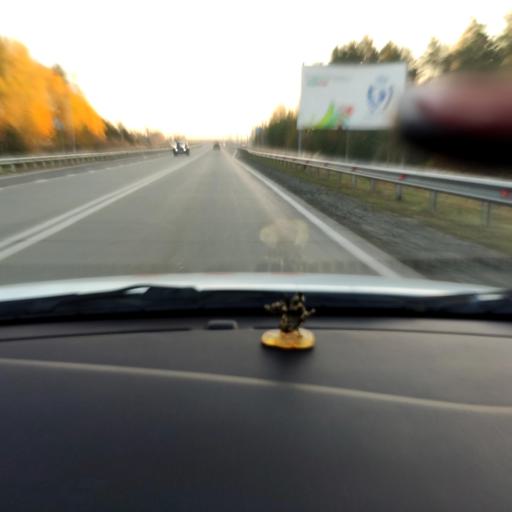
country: RU
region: Tatarstan
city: Stolbishchi
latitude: 55.6775
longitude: 49.1890
